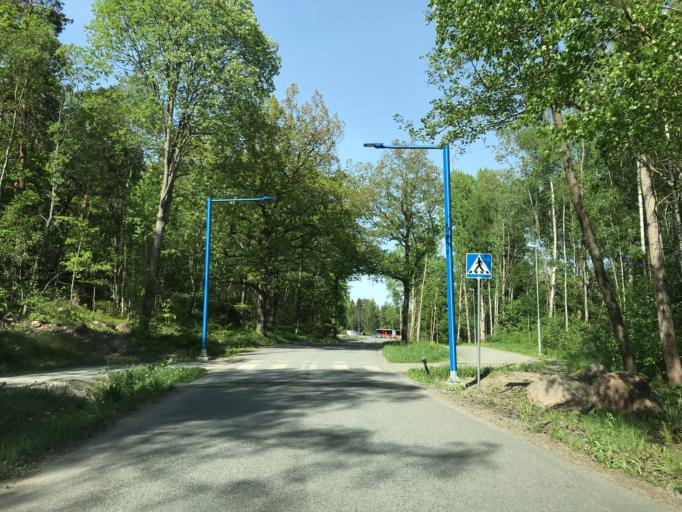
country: SE
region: Stockholm
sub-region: Sollentuna Kommun
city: Sollentuna
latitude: 59.4323
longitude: 17.9910
